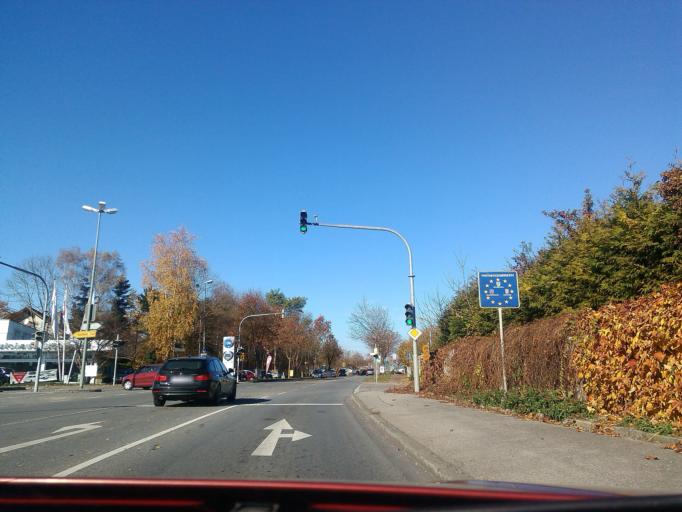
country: DE
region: Bavaria
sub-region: Upper Bavaria
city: Grobenzell
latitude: 48.1825
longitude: 11.3890
